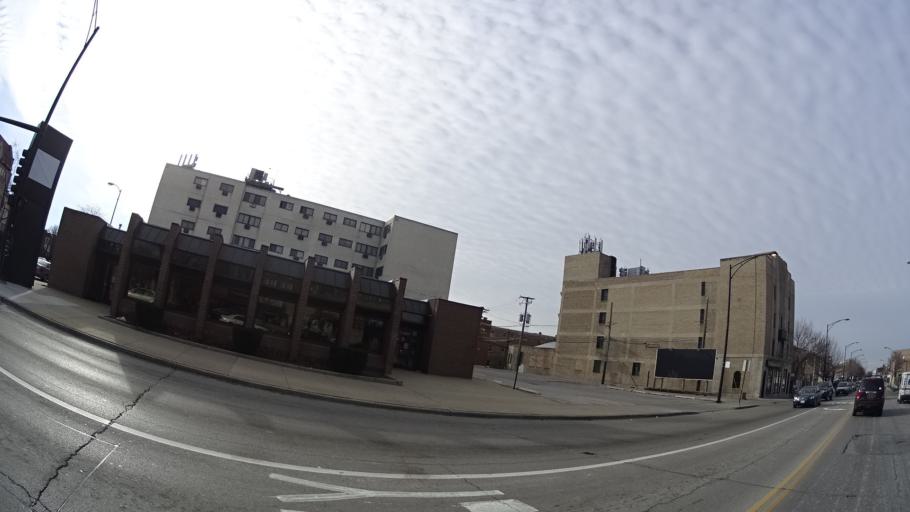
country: US
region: Illinois
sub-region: Cook County
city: Evanston
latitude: 42.0196
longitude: -87.6849
